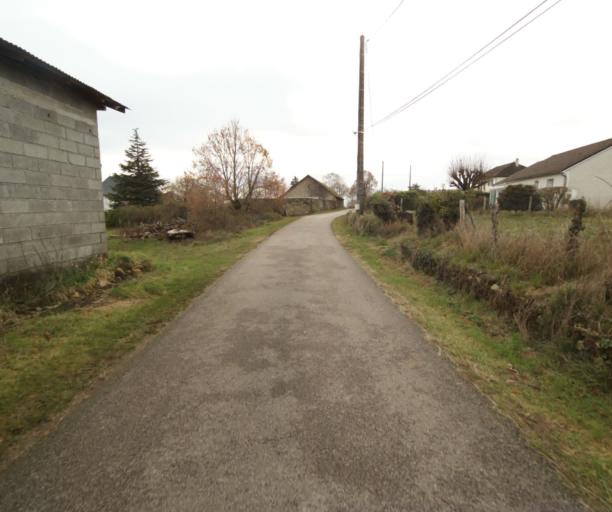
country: FR
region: Limousin
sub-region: Departement de la Correze
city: Saint-Mexant
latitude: 45.2538
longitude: 1.6600
